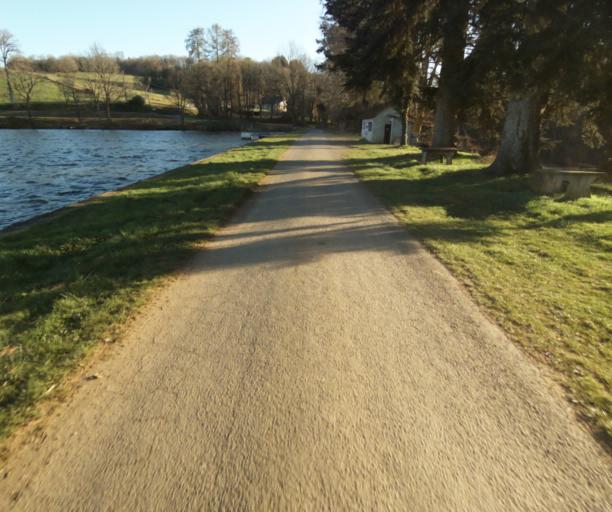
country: FR
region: Limousin
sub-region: Departement de la Correze
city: Seilhac
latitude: 45.3688
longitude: 1.6925
